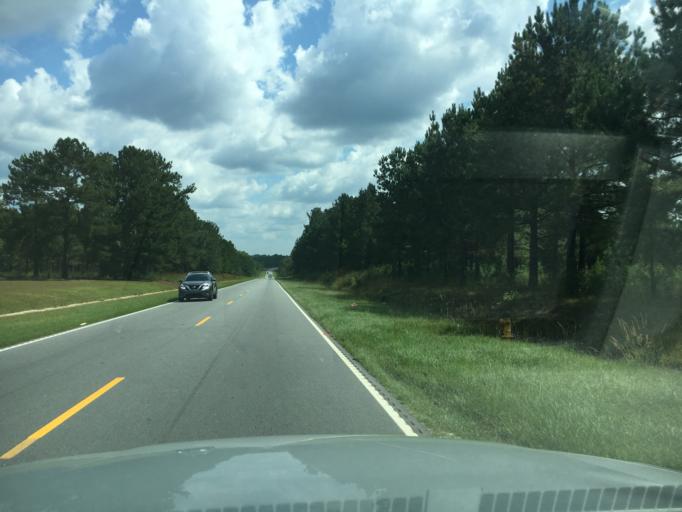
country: US
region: South Carolina
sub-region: Greenwood County
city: Greenwood
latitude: 34.1550
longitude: -82.1687
